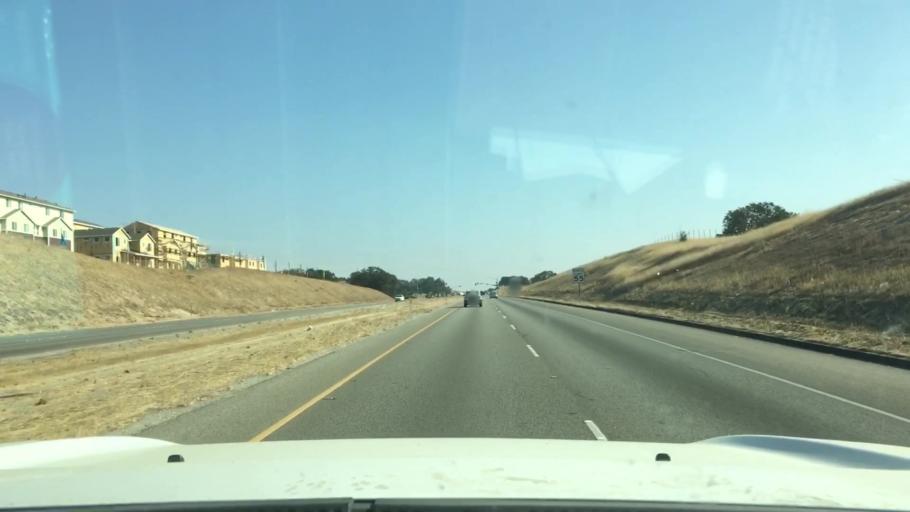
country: US
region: California
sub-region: San Luis Obispo County
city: Paso Robles
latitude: 35.6445
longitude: -120.6780
